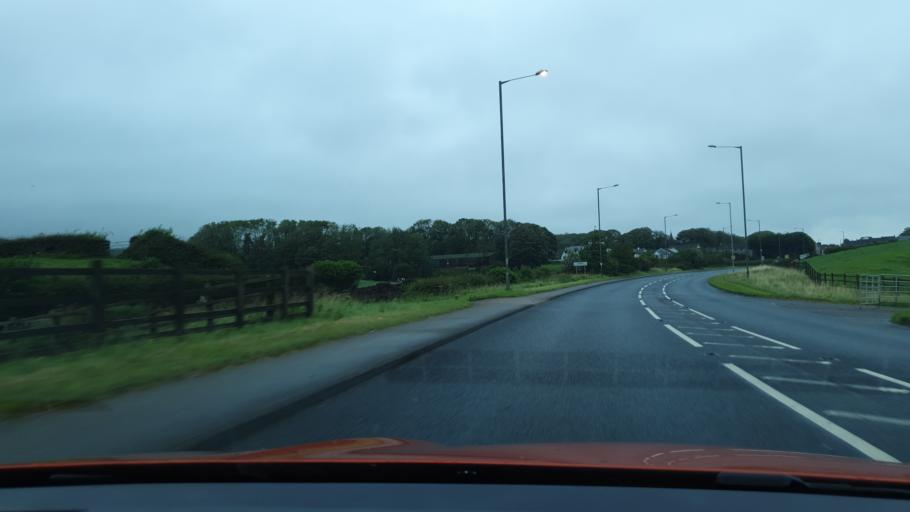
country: GB
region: England
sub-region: Cumbria
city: Dalton in Furness
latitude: 54.1702
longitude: -3.1564
